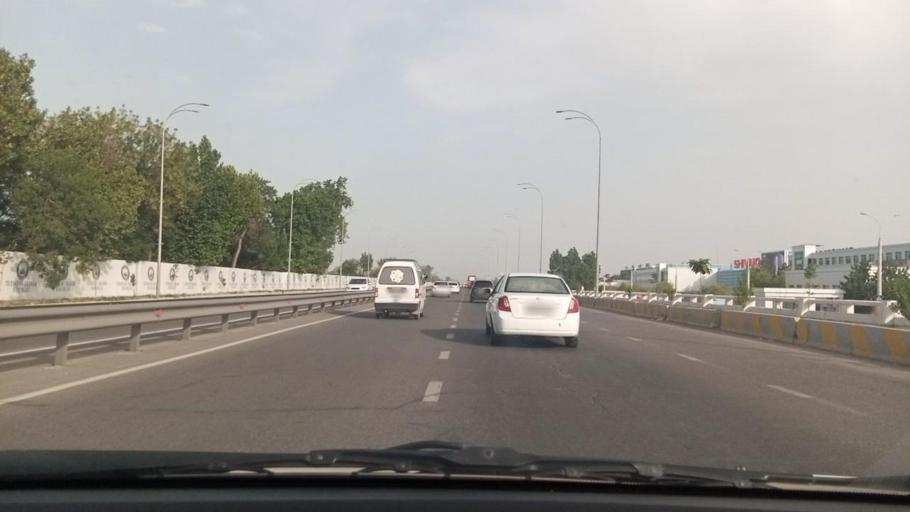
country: UZ
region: Toshkent Shahri
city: Bektemir
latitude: 41.2659
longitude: 69.3690
